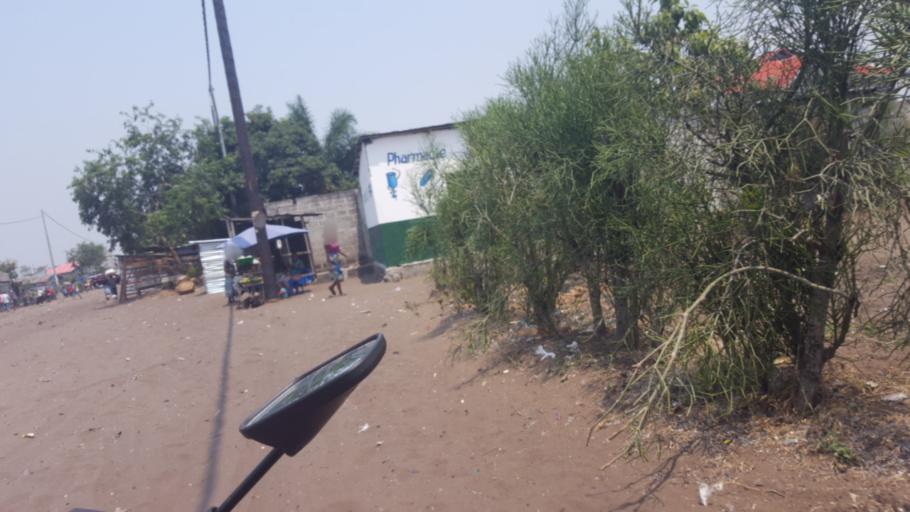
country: CD
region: Kinshasa
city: Masina
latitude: -4.3609
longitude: 15.5080
